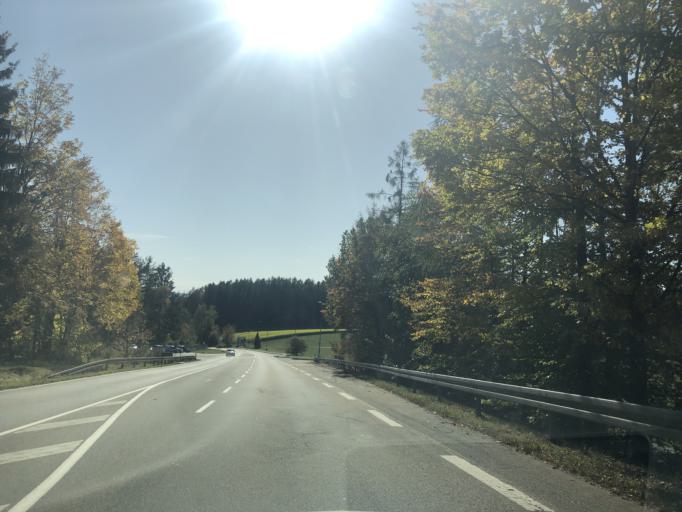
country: DE
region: Bavaria
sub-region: Lower Bavaria
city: Regen
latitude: 48.9899
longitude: 13.1348
